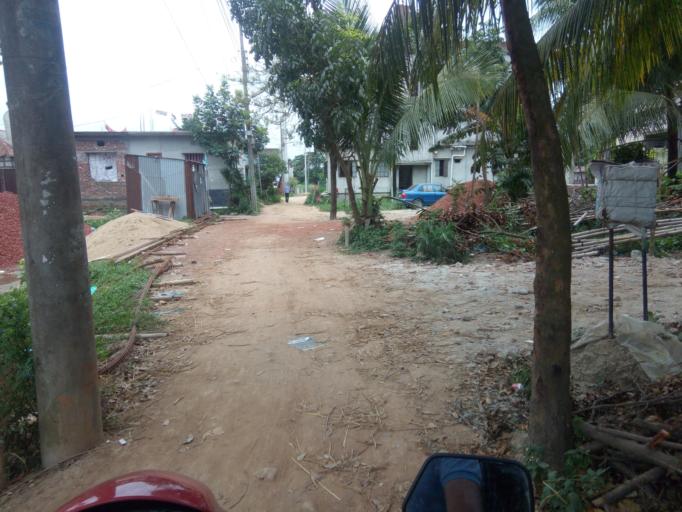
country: BD
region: Dhaka
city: Paltan
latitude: 23.7351
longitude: 90.4510
